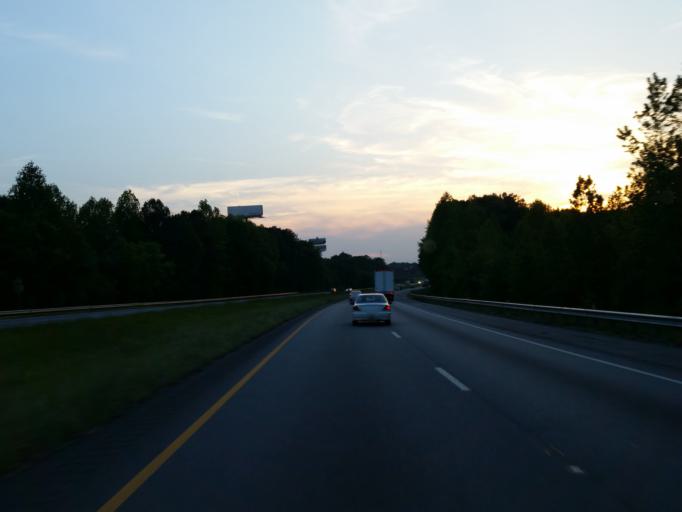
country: US
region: Alabama
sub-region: Cleburne County
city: Heflin
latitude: 33.6204
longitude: -85.5865
